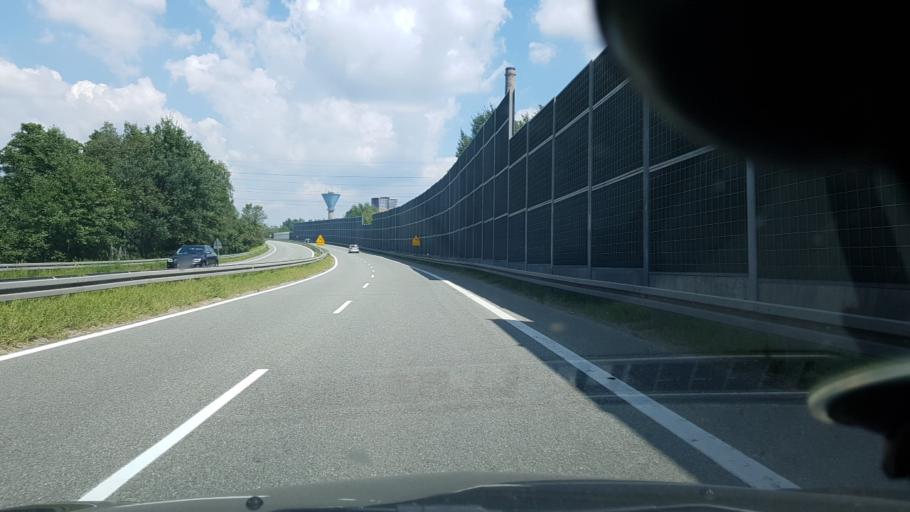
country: PL
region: Silesian Voivodeship
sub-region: Powiat mikolowski
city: Laziska Gorne
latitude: 50.1302
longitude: 18.8267
